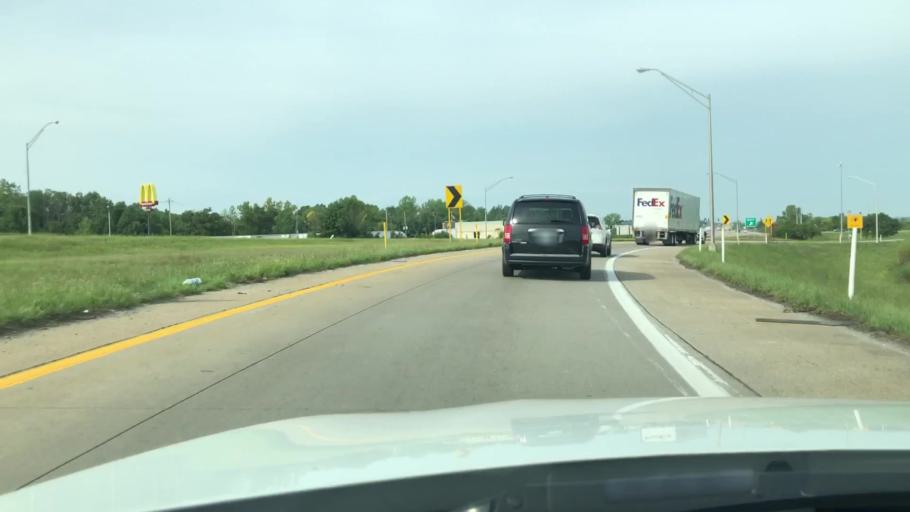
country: US
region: Kentucky
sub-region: Jefferson County
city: Heritage Creek
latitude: 38.1375
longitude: -85.7097
